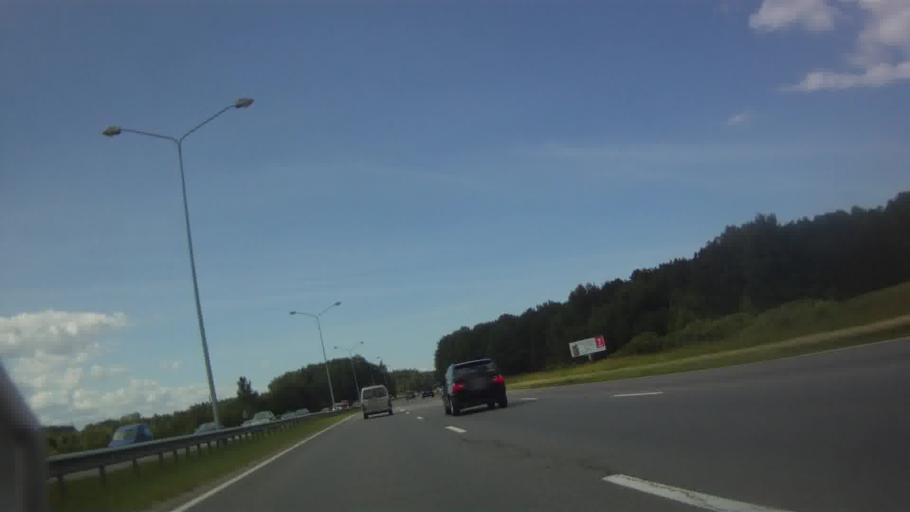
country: LV
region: Babite
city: Pinki
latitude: 56.9626
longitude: 23.8812
